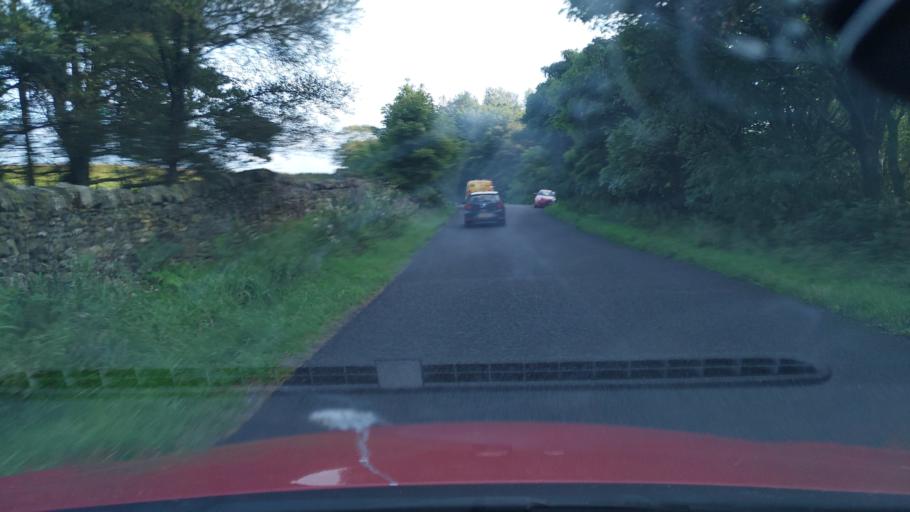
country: GB
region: England
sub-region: Blackburn with Darwen
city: Darwen
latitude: 53.6818
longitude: -2.5101
